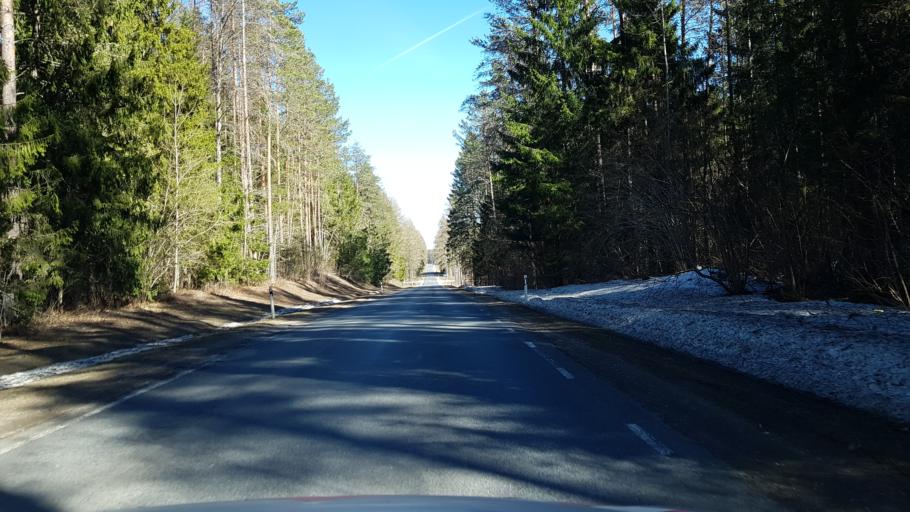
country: EE
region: Laeaene-Virumaa
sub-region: Vinni vald
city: Vinni
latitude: 59.2737
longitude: 26.6254
